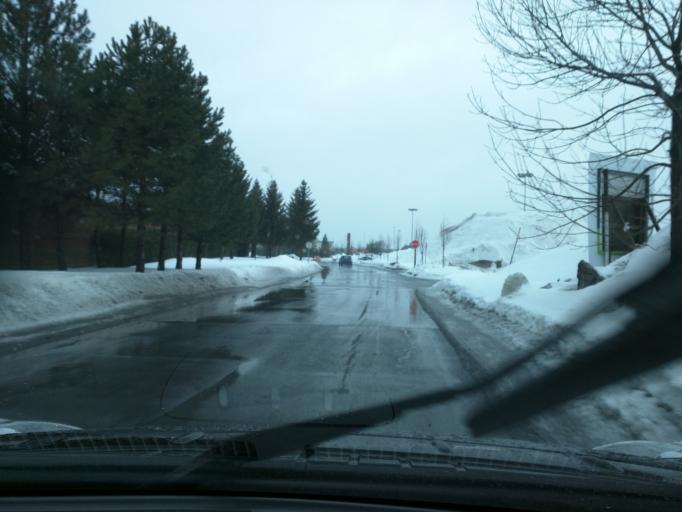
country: CA
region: Quebec
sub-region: Monteregie
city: Longueuil
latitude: 45.5377
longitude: -73.4666
